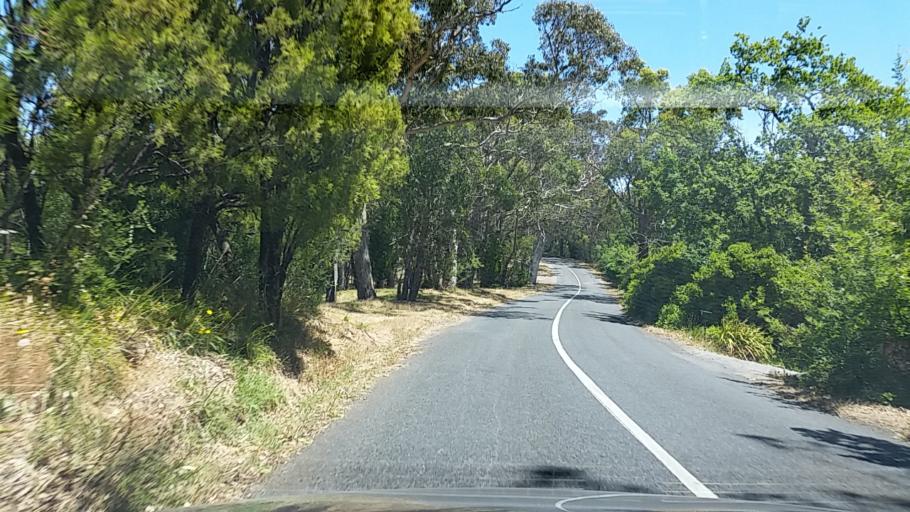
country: AU
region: South Australia
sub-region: Adelaide Hills
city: Crafers
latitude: -34.9978
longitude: 138.6909
